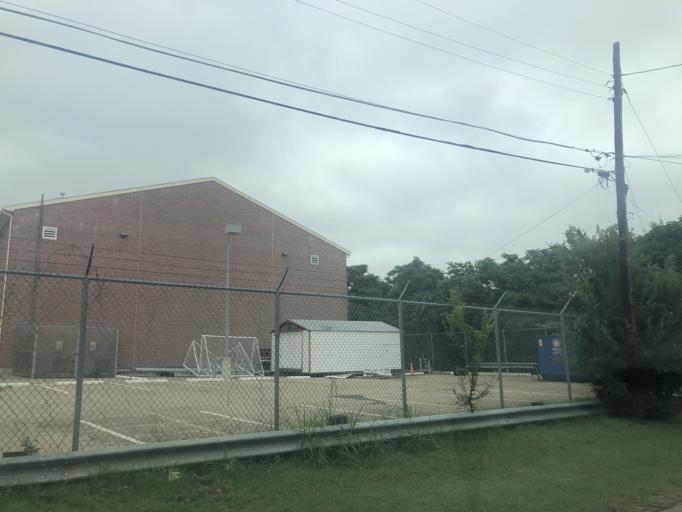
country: US
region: Texas
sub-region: Dallas County
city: Dallas
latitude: 32.7765
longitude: -96.8471
